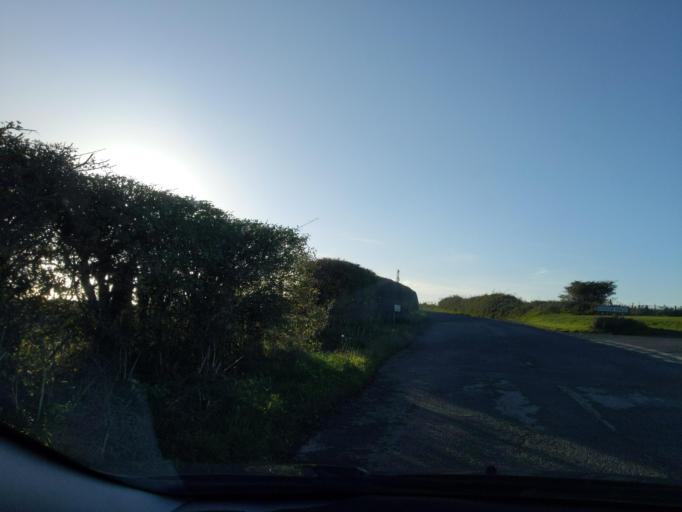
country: GB
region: England
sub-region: Plymouth
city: Plymstock
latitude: 50.3456
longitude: -4.1044
